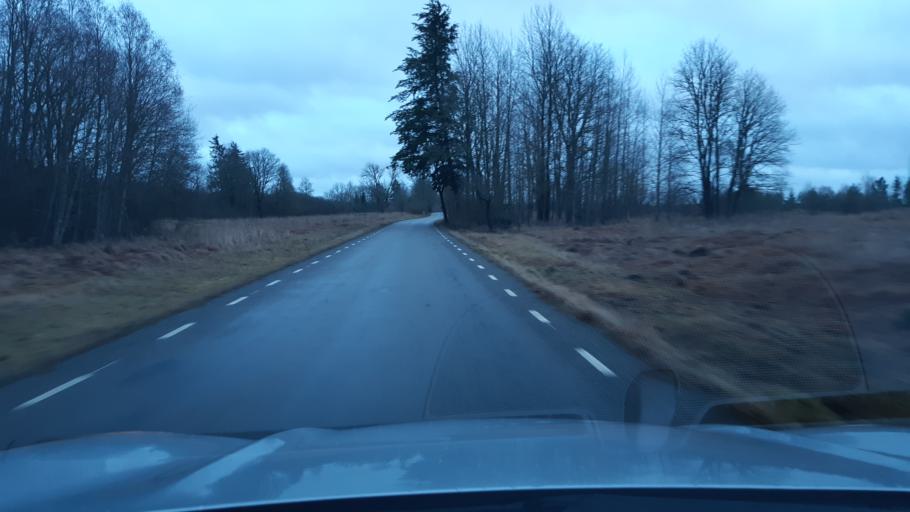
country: EE
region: Raplamaa
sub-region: Rapla vald
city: Rapla
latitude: 58.9933
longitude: 24.7229
